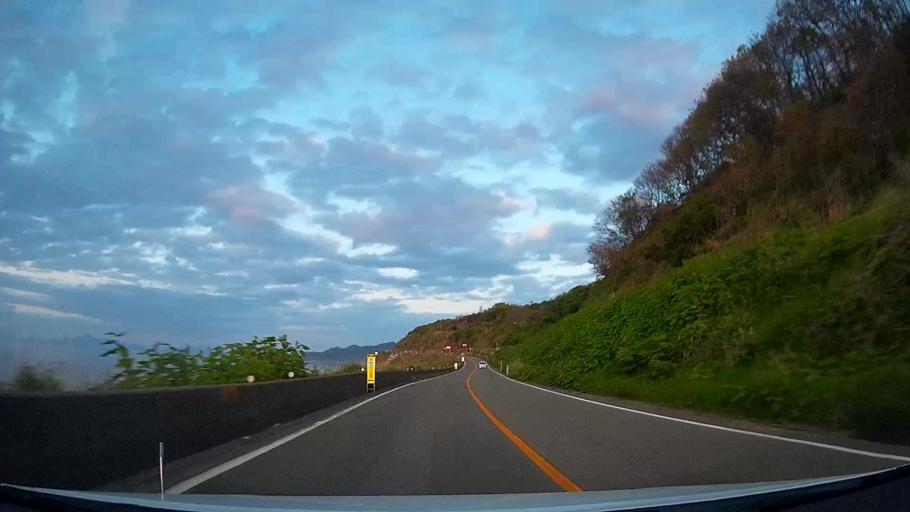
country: JP
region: Niigata
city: Joetsu
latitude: 37.1718
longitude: 138.1122
